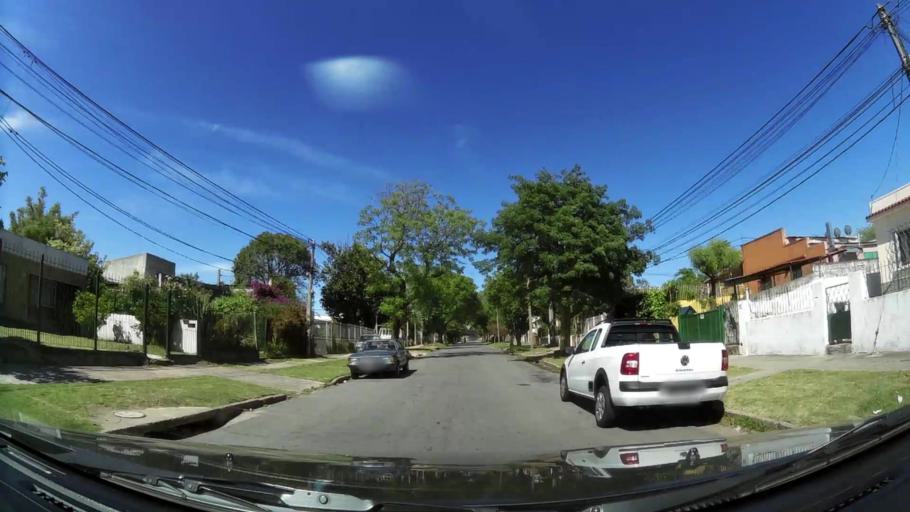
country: UY
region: Canelones
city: Paso de Carrasco
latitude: -34.8655
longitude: -56.1184
